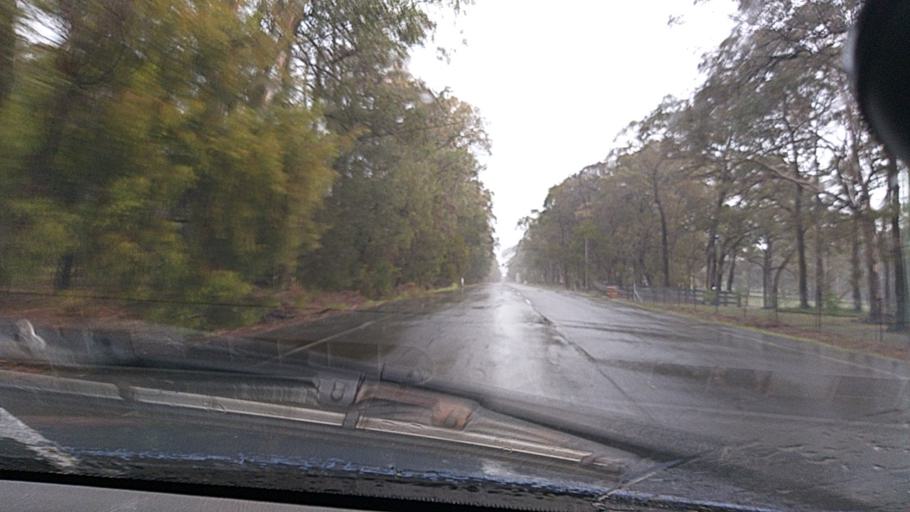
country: AU
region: New South Wales
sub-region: Wollondilly
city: Douglas Park
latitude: -34.2453
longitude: 150.7270
